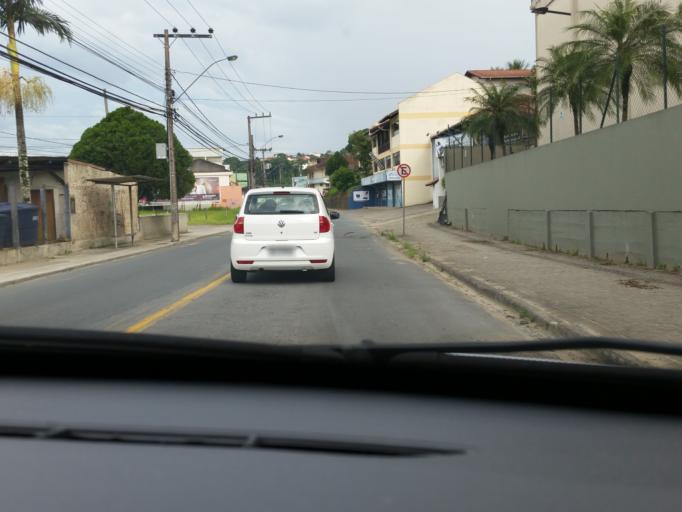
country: BR
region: Santa Catarina
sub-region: Blumenau
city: Blumenau
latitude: -26.9111
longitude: -49.1044
